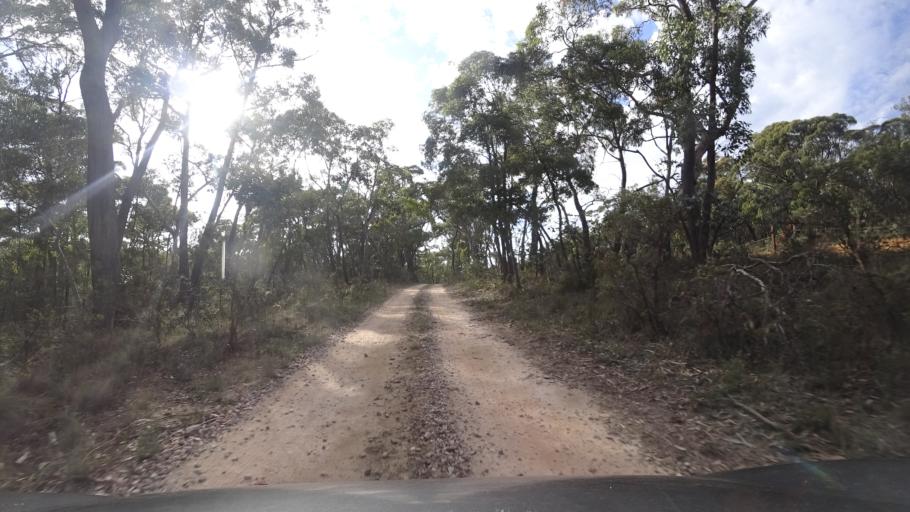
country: AU
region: New South Wales
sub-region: Lithgow
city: Lithgow
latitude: -33.4758
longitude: 150.2435
